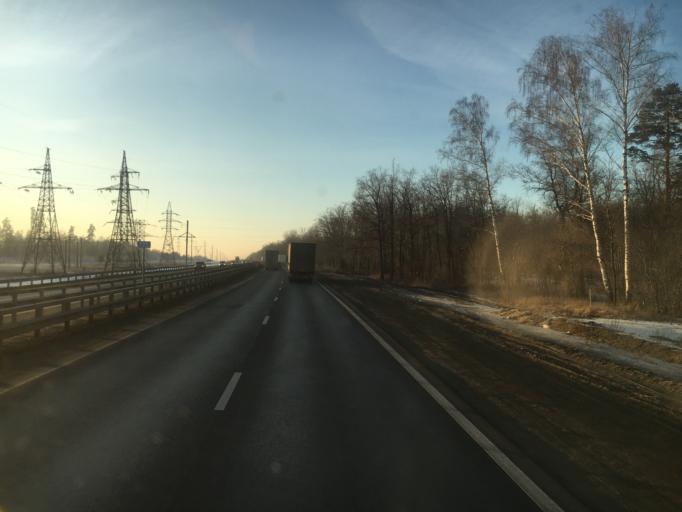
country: RU
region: Samara
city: Pribrezhnyy
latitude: 53.5186
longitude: 49.8206
